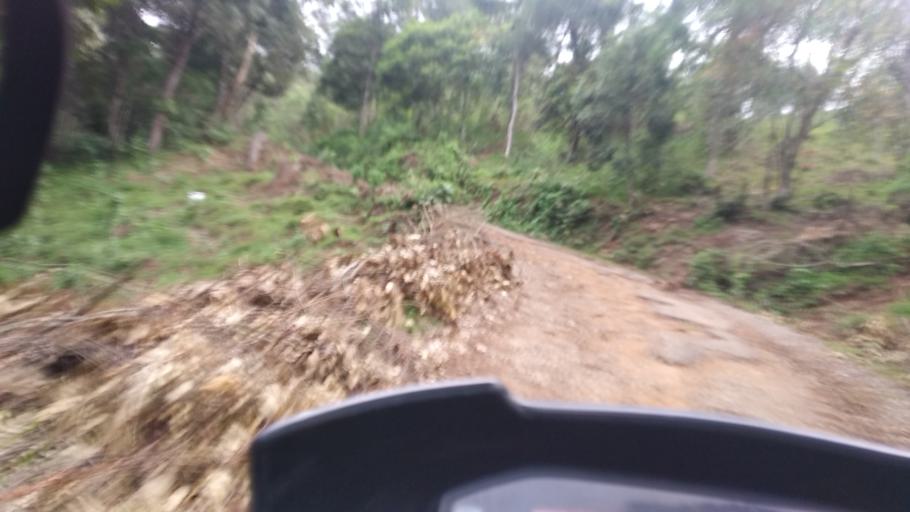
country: IN
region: Tamil Nadu
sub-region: Theni
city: Gudalur
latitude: 9.5500
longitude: 77.0568
